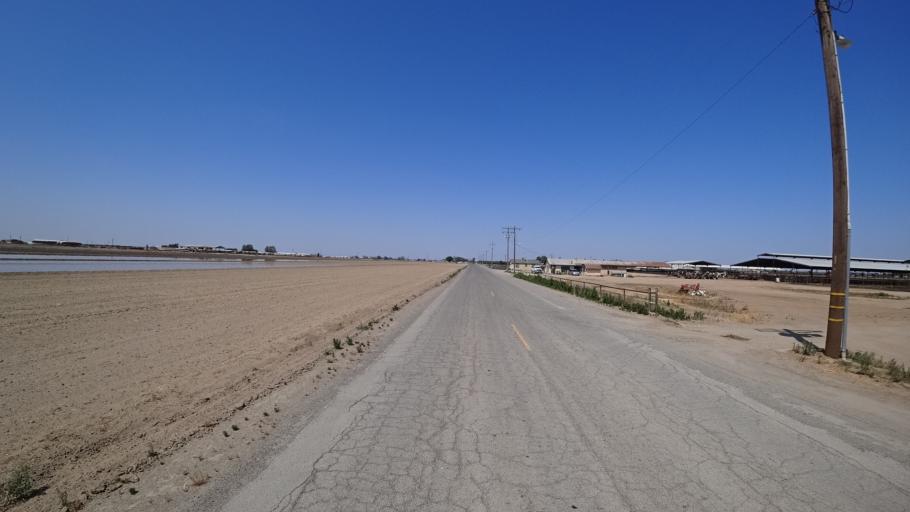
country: US
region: California
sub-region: Kings County
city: Home Garden
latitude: 36.2839
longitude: -119.6126
